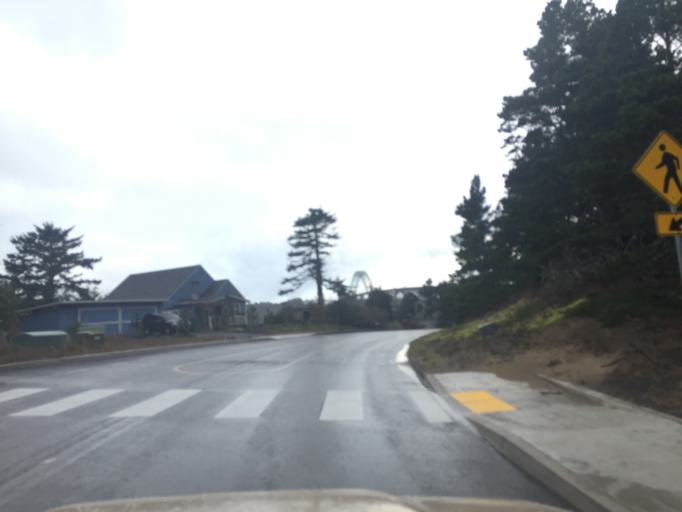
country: US
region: Oregon
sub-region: Lincoln County
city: Newport
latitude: 44.6164
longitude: -124.0524
